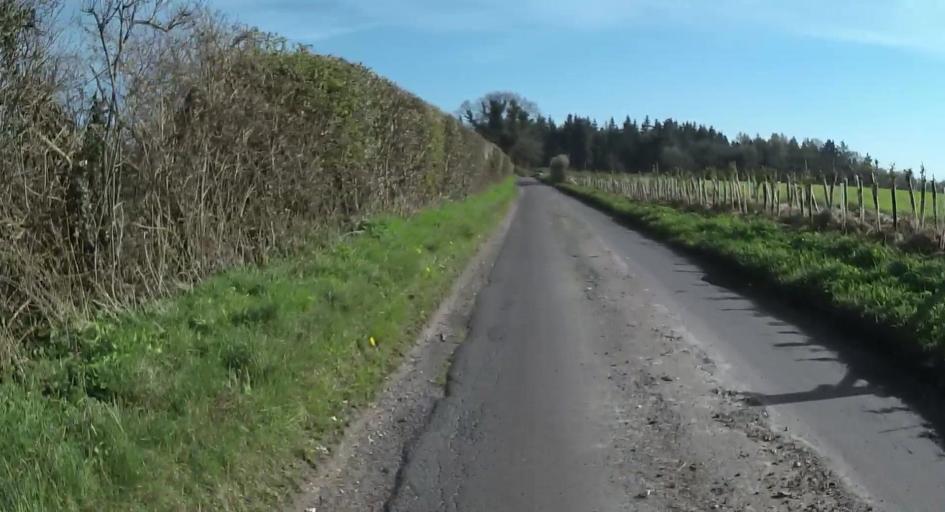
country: GB
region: England
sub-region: Hampshire
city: Highclere
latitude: 51.2571
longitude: -1.3673
